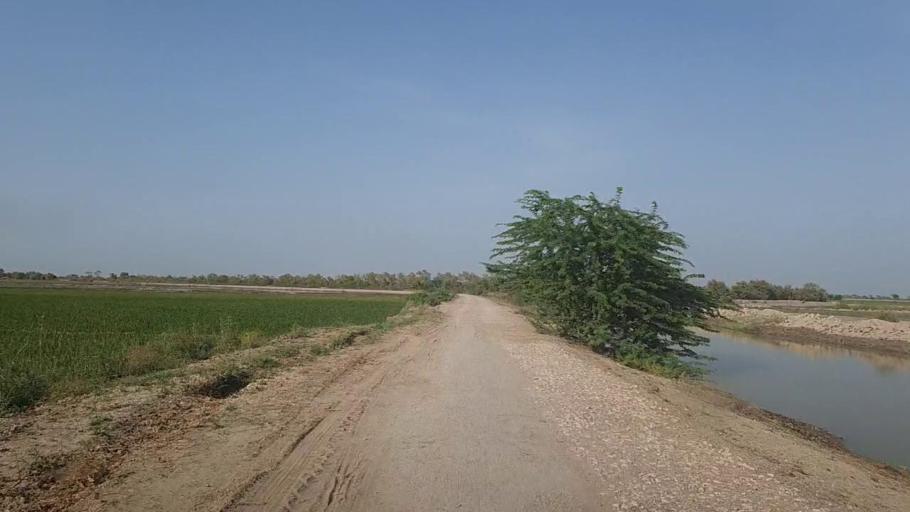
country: PK
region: Sindh
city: Sita Road
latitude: 27.0959
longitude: 67.8718
